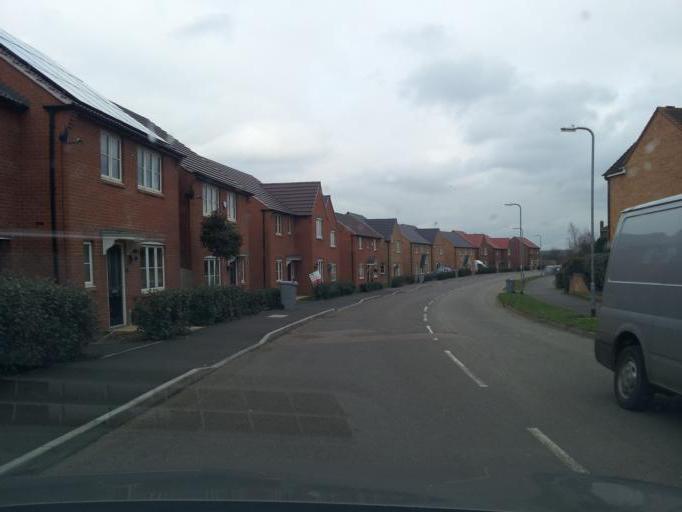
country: GB
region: England
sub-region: Lincolnshire
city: Great Gonerby
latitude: 52.9193
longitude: -0.6608
